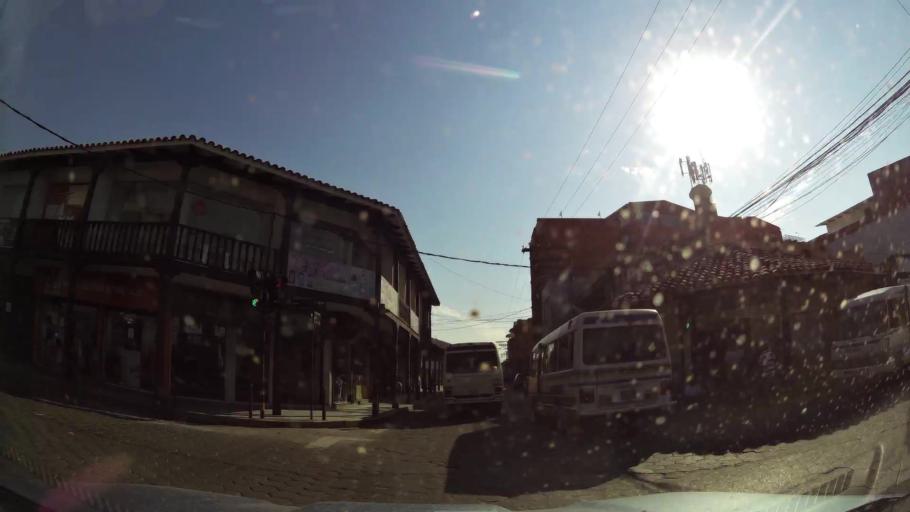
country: BO
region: Santa Cruz
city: Santa Cruz de la Sierra
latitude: -17.7805
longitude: -63.1788
